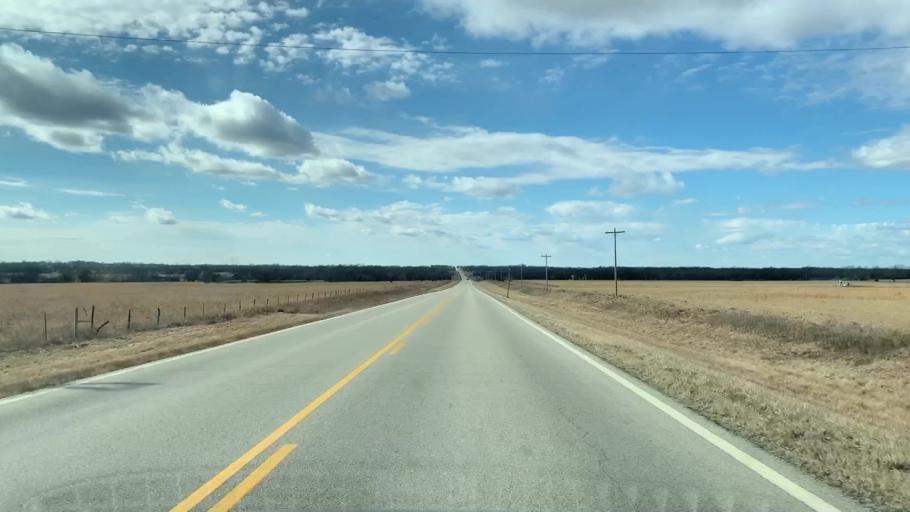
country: US
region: Kansas
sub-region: Neosho County
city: Erie
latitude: 37.5291
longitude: -95.3890
